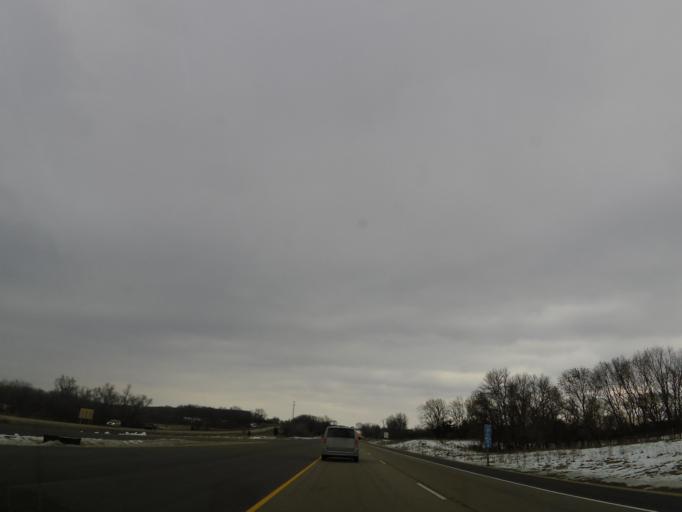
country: US
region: Wisconsin
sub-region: Rock County
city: Edgerton
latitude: 42.8641
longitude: -89.0459
